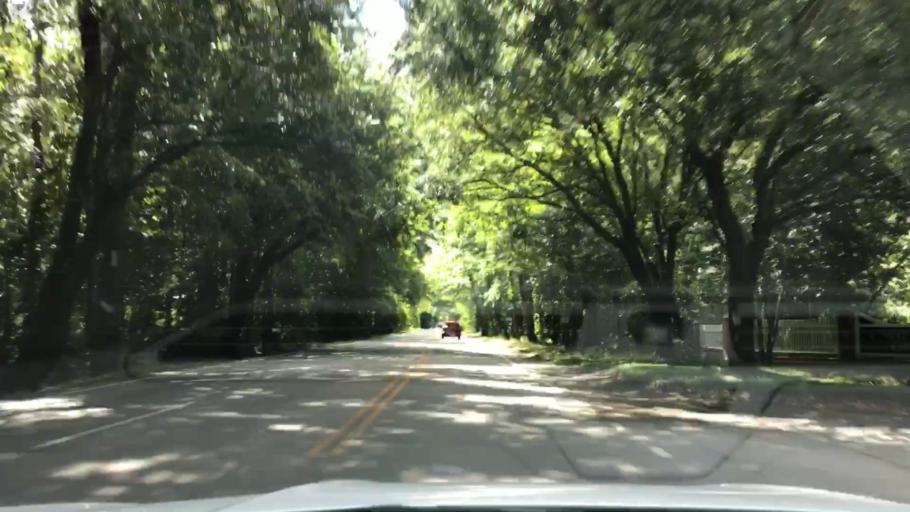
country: US
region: South Carolina
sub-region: Charleston County
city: Shell Point
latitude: 32.8594
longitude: -80.0768
